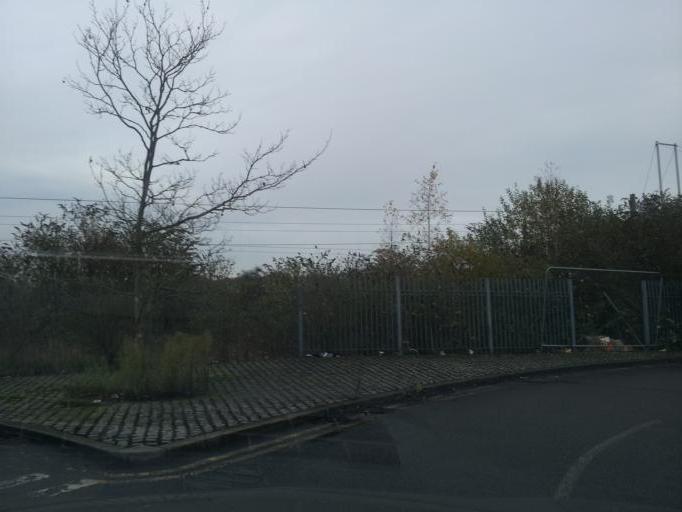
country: GB
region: England
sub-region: Essex
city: Rowhedge
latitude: 51.8790
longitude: 0.9343
